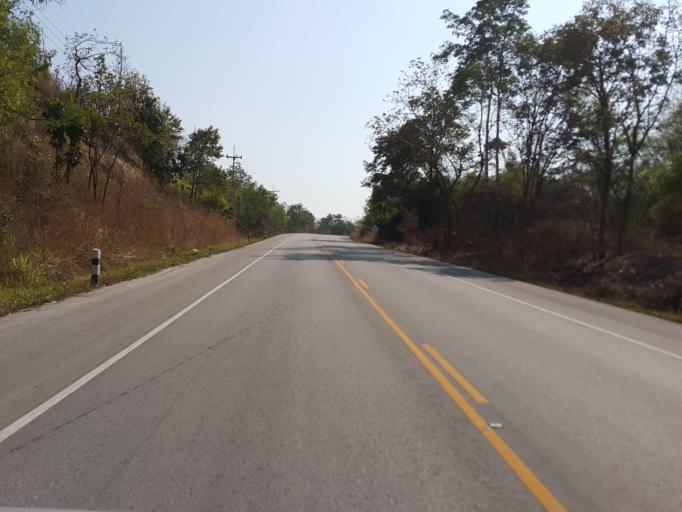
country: TH
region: Lampang
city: Mueang Pan
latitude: 18.8091
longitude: 99.5900
